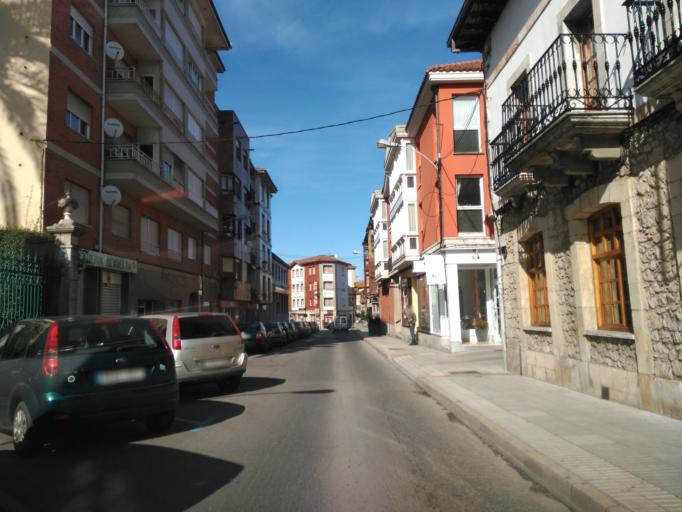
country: ES
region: Asturias
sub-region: Province of Asturias
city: Llanes
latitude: 43.4177
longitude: -4.7536
